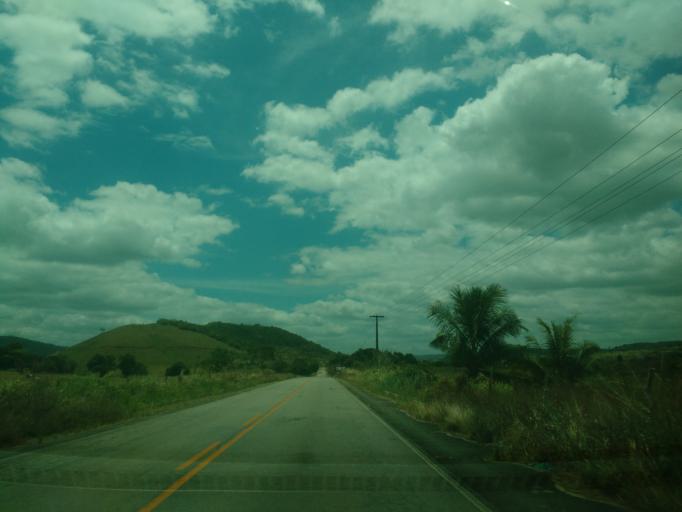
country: BR
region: Alagoas
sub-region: Uniao Dos Palmares
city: Uniao dos Palmares
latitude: -9.1426
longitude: -36.0774
